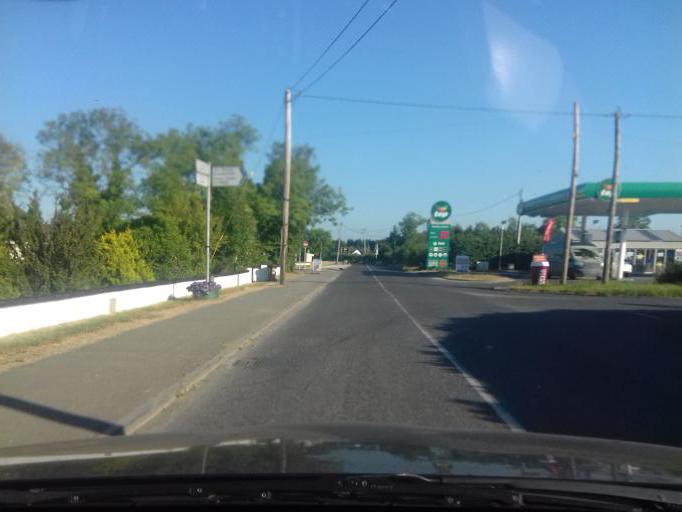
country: IE
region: Leinster
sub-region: An Mhi
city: Ashbourne
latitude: 53.4511
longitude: -6.3952
